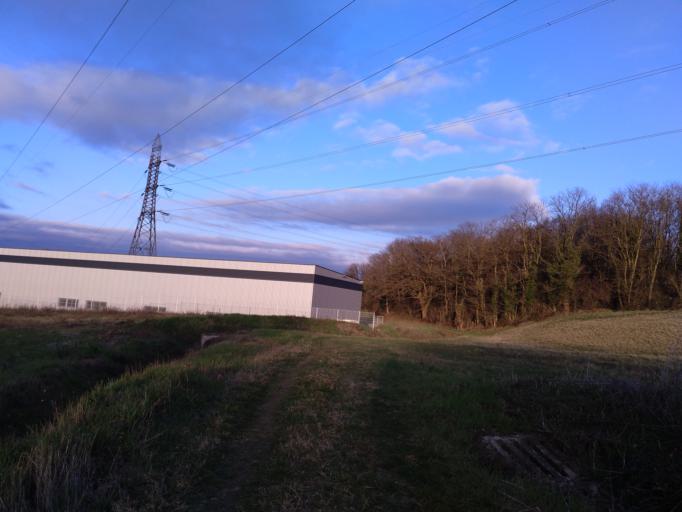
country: FR
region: Rhone-Alpes
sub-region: Departement du Rhone
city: Mions
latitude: 45.6650
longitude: 4.9689
